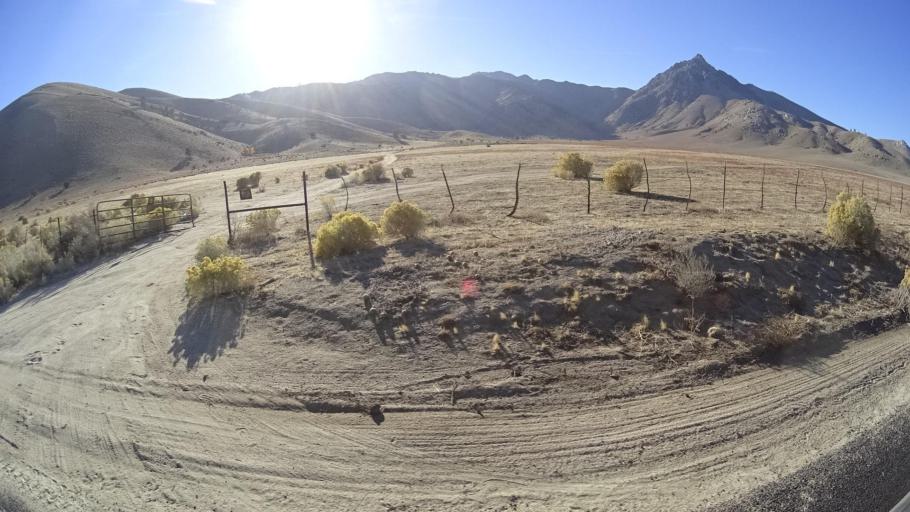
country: US
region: California
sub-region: Kern County
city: Weldon
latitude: 35.6184
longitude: -118.2540
